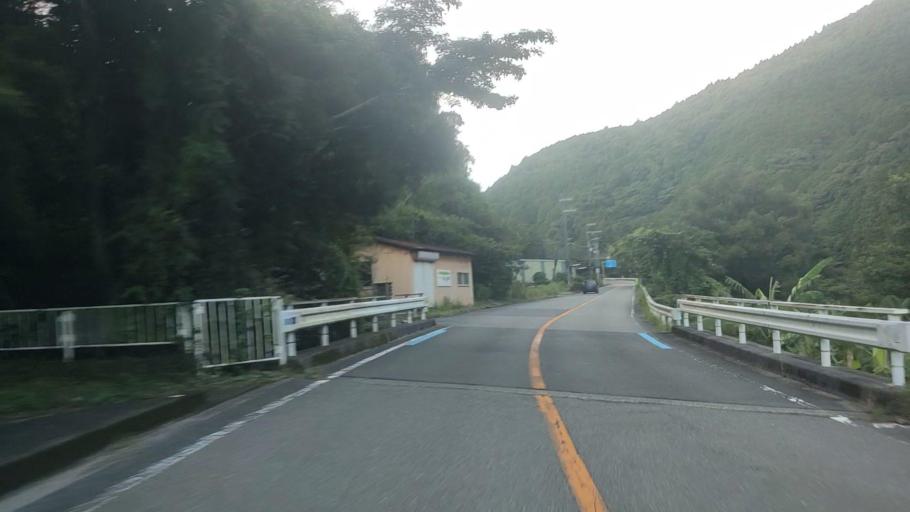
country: JP
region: Wakayama
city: Tanabe
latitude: 33.8140
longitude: 135.5513
